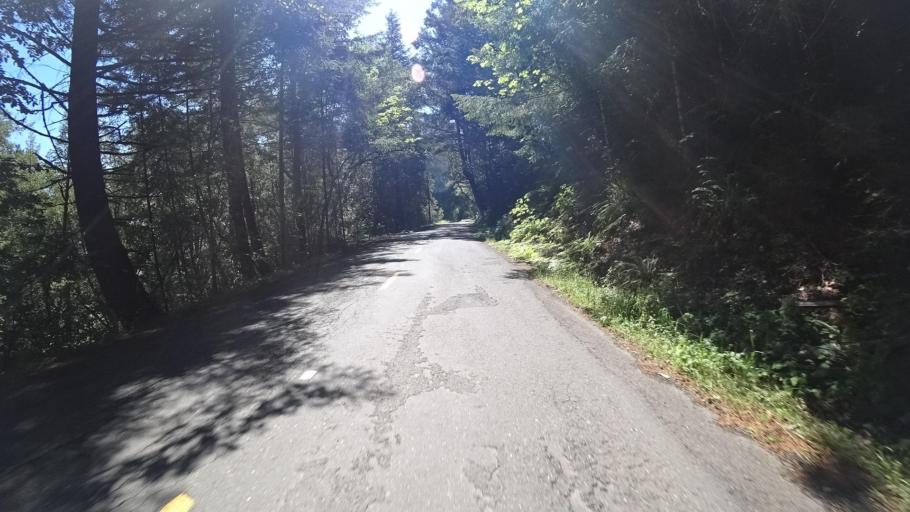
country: US
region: California
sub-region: Humboldt County
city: Rio Dell
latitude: 40.2314
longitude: -124.1531
